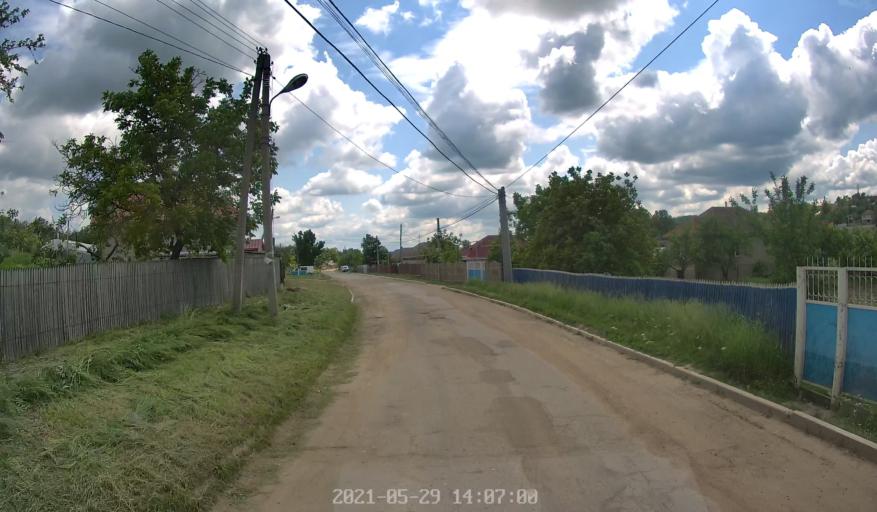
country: MD
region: Hincesti
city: Hincesti
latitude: 46.8327
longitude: 28.6758
